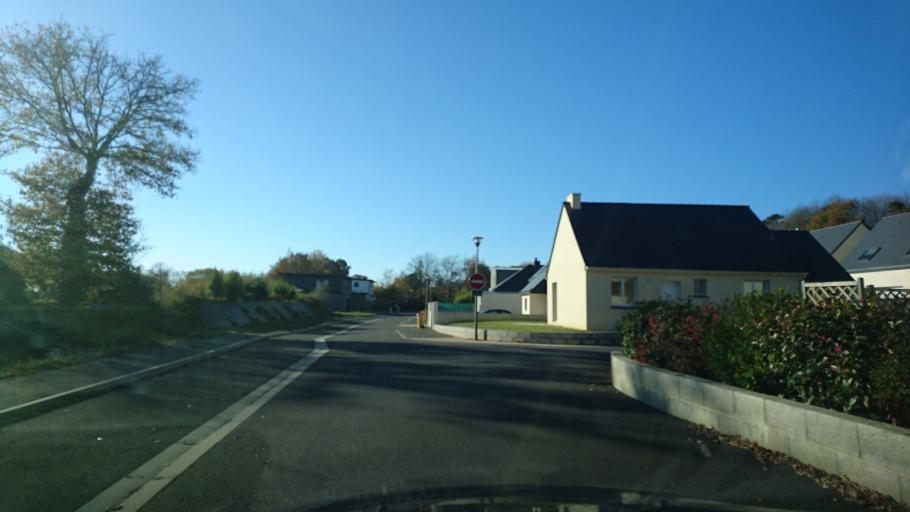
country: FR
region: Brittany
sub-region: Departement des Cotes-d'Armor
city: Pledran
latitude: 48.4523
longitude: -2.7432
